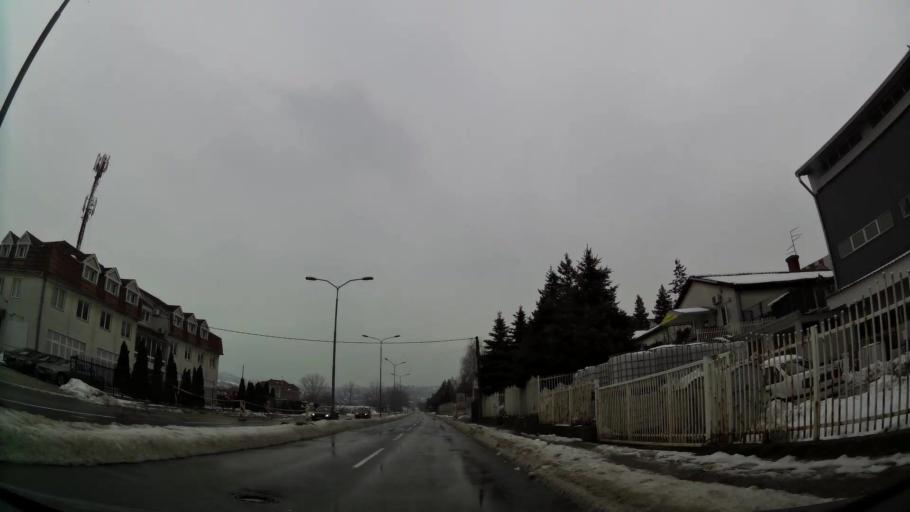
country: RS
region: Central Serbia
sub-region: Belgrade
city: Vozdovac
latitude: 44.7555
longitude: 20.4982
